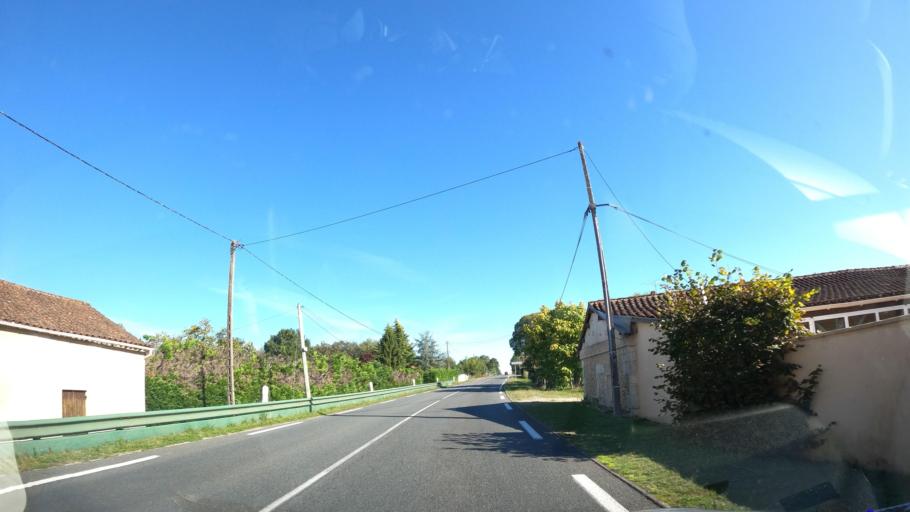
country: FR
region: Aquitaine
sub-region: Departement de la Dordogne
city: Vergt
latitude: 45.0196
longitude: 0.6118
